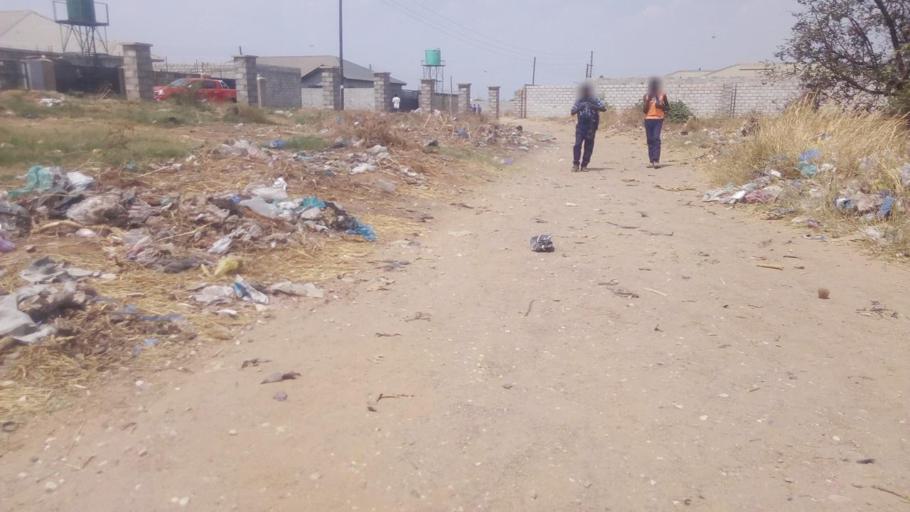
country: ZM
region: Lusaka
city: Lusaka
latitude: -15.3665
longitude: 28.2899
